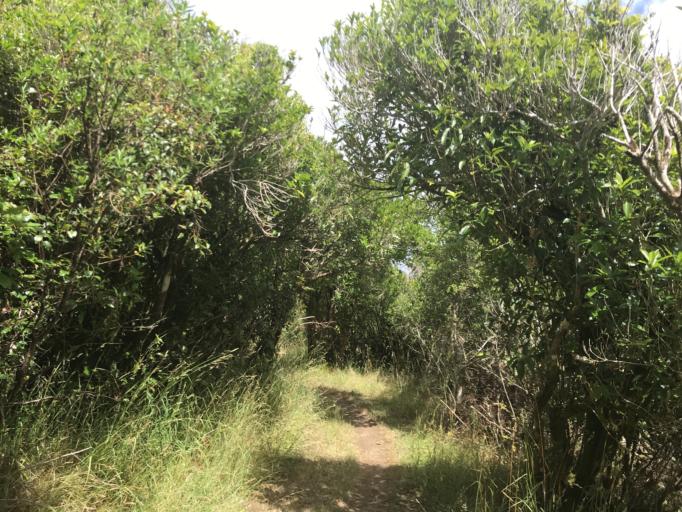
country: NZ
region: Marlborough
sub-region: Marlborough District
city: Picton
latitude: -41.2104
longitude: 174.0162
